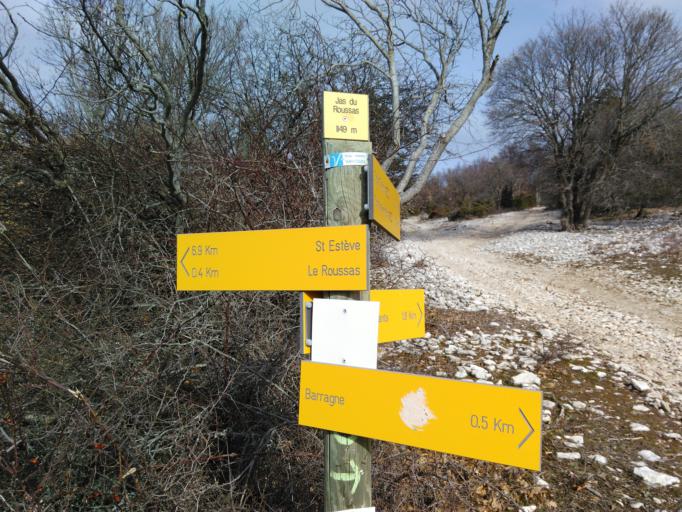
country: FR
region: Provence-Alpes-Cote d'Azur
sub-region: Departement du Vaucluse
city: Villes-sur-Auzon
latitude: 44.1365
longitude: 5.2900
